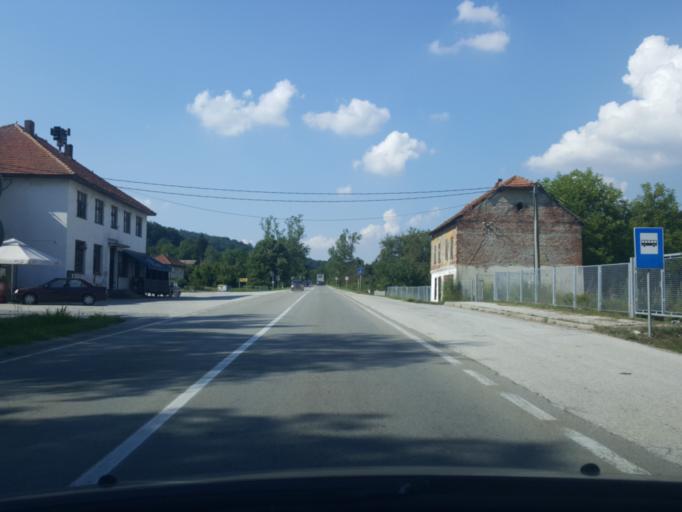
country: RS
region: Central Serbia
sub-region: Moravicki Okrug
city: Gornji Milanovac
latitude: 44.0930
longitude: 20.4807
